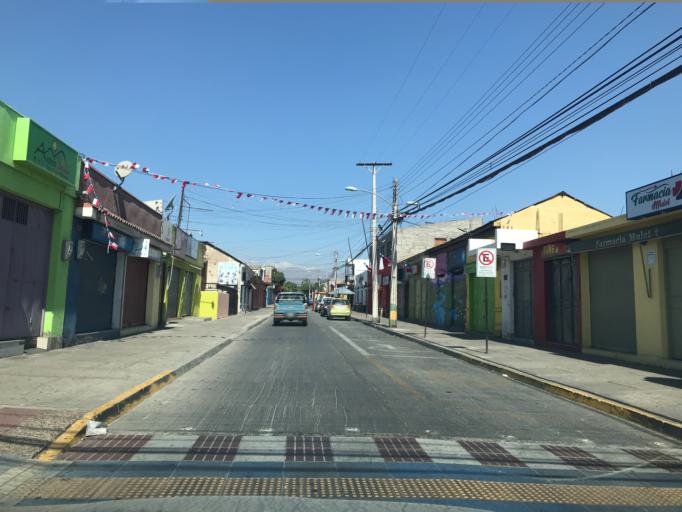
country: CL
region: Atacama
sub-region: Provincia de Huasco
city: Vallenar
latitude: -28.5781
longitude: -70.7563
